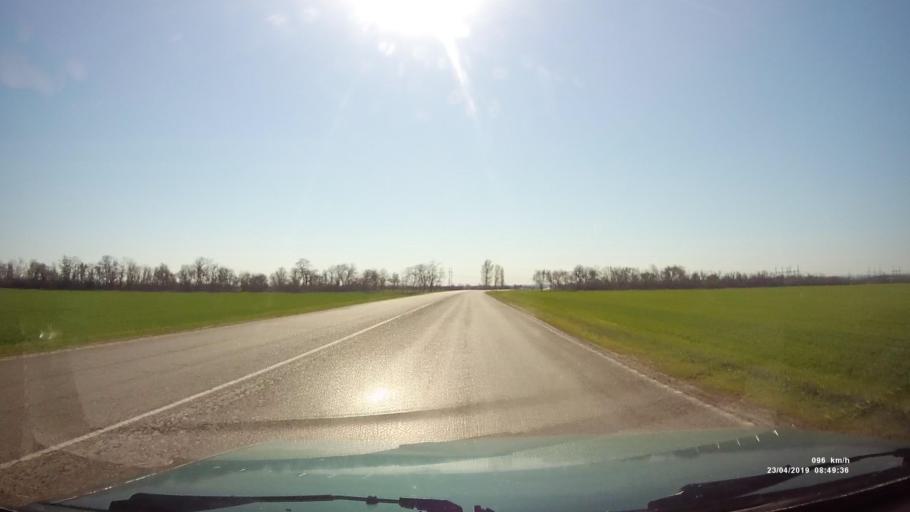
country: RU
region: Rostov
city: Gigant
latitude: 46.5039
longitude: 41.4132
